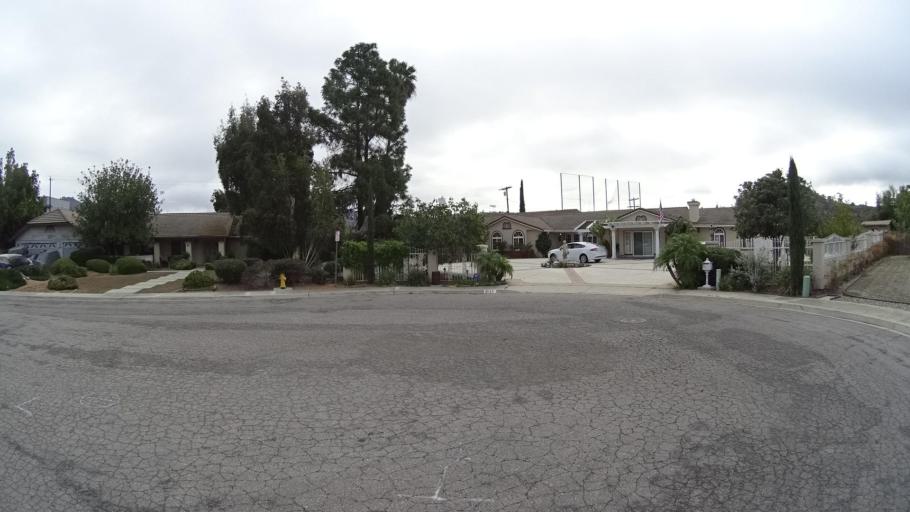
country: US
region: California
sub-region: San Diego County
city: Rancho San Diego
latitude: 32.7589
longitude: -116.9232
